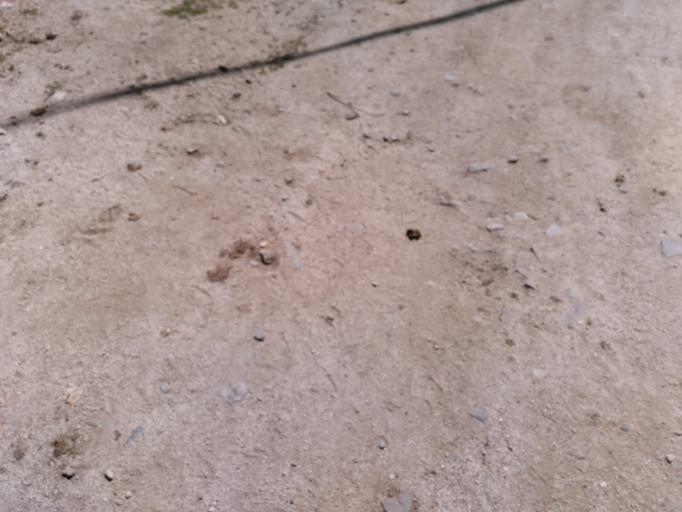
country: RU
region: Bashkortostan
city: Akhunovo
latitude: 54.2078
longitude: 59.5999
